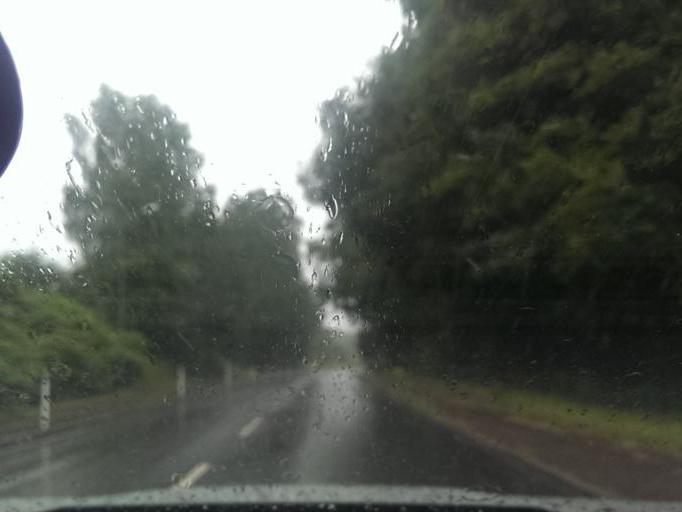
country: SE
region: Skane
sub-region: Orkelljunga Kommun
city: OErkelljunga
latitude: 56.2932
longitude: 13.2820
